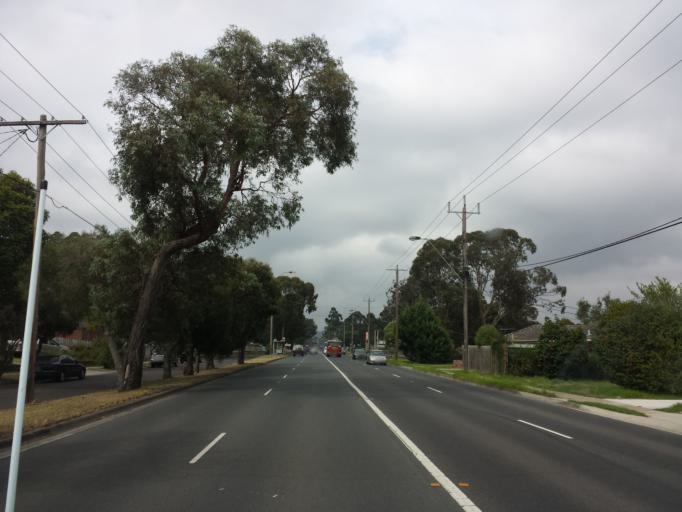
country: AU
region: Victoria
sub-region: Knox
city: Boronia
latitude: -37.8728
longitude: 145.2850
